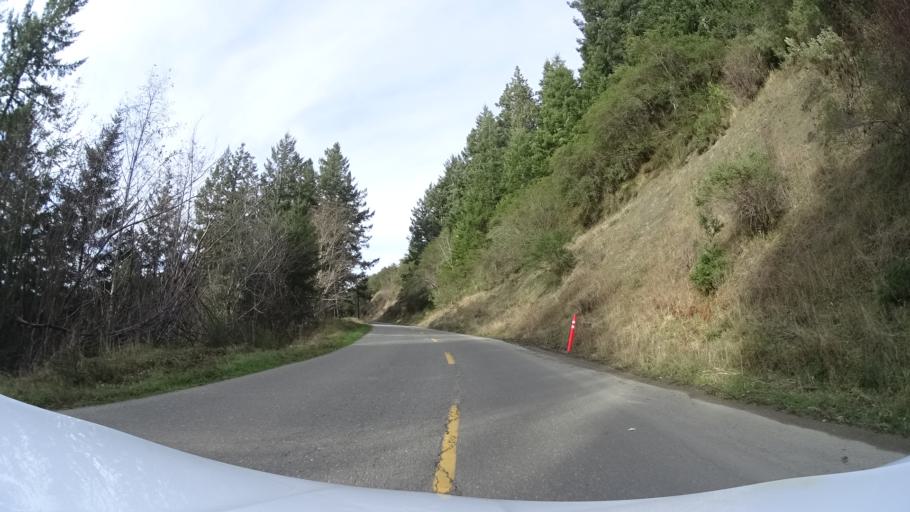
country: US
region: California
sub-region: Humboldt County
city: Ferndale
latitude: 40.5320
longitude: -124.2682
